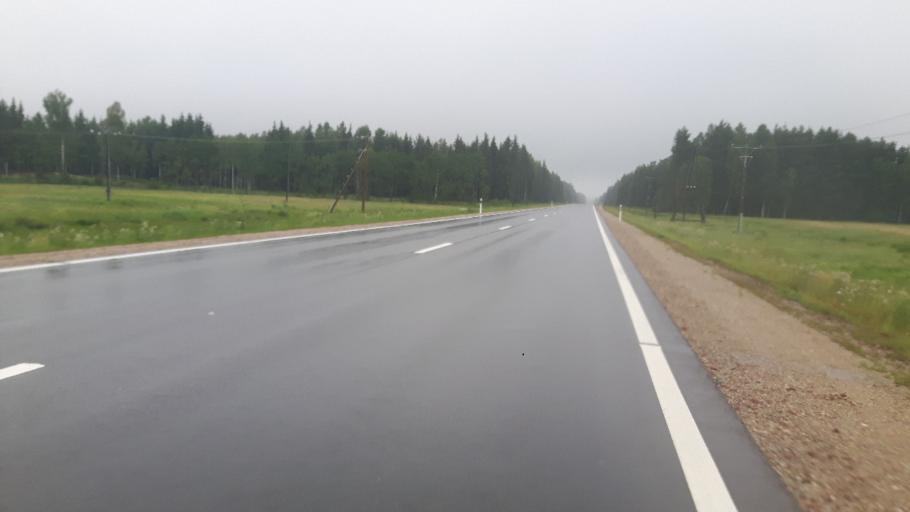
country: LV
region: Rucavas
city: Rucava
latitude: 56.1646
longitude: 21.1455
